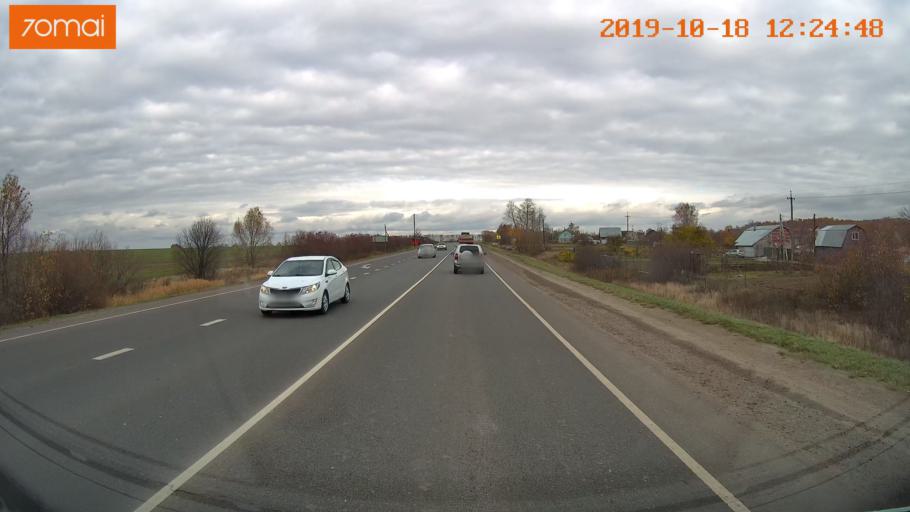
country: RU
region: Rjazan
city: Rybnoye
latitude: 54.5427
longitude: 39.5152
